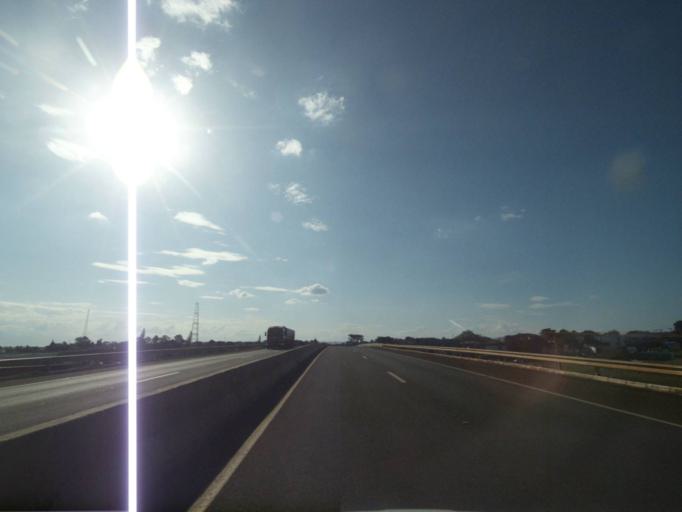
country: BR
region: Parana
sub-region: Londrina
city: Londrina
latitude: -23.3605
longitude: -51.1515
